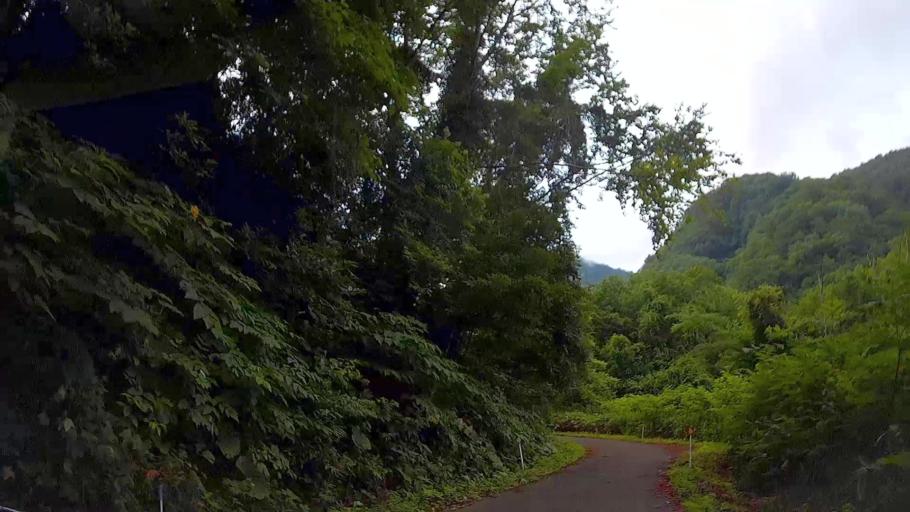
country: JP
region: Hokkaido
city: Nanae
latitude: 42.0515
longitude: 140.4946
